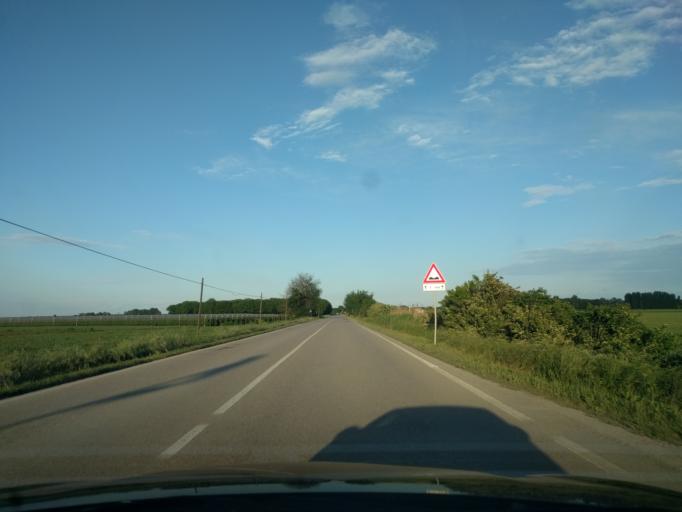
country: IT
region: Veneto
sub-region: Provincia di Rovigo
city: Guarda Veneta
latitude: 44.9831
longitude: 11.8276
